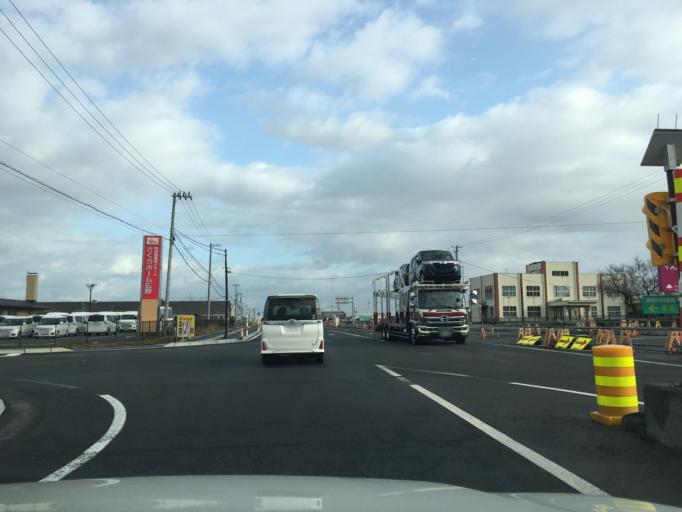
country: JP
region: Yamagata
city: Sakata
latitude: 38.8483
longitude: 139.8486
